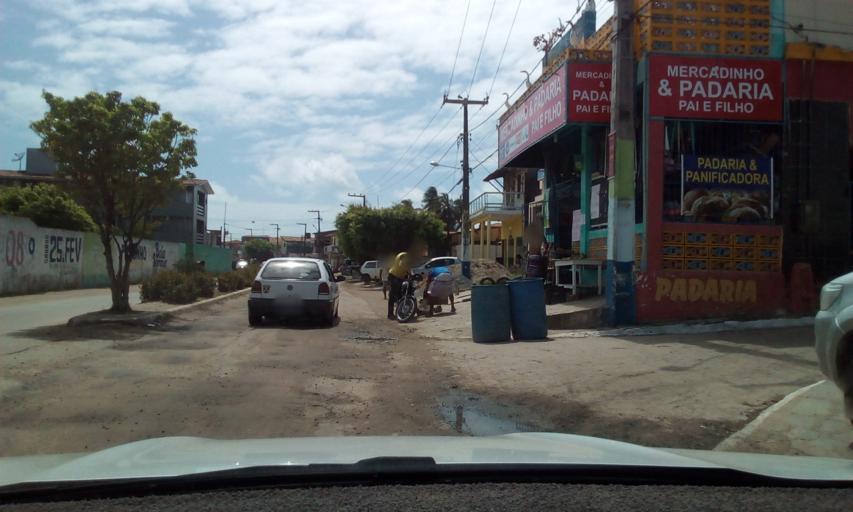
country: BR
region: Paraiba
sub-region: Rio Tinto
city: Rio Tinto
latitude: -6.6912
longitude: -34.9345
